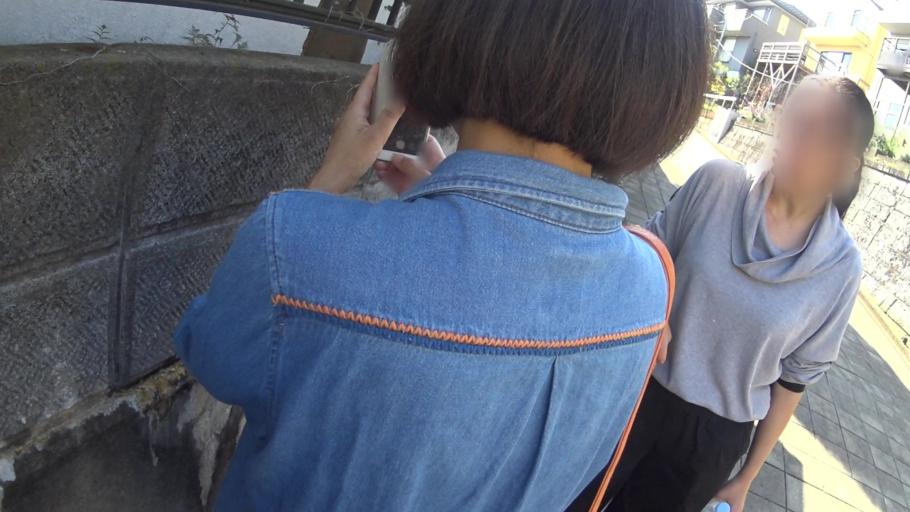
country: JP
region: Tokyo
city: Chofugaoka
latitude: 35.5860
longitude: 139.5525
